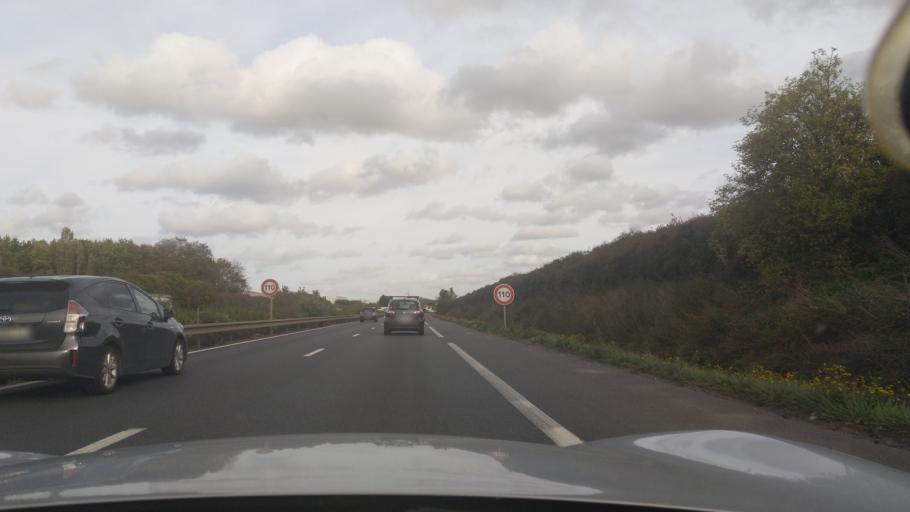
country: FR
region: Ile-de-France
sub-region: Departement du Val-d'Oise
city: Auvers-sur-Oise
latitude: 49.0518
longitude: 2.1543
